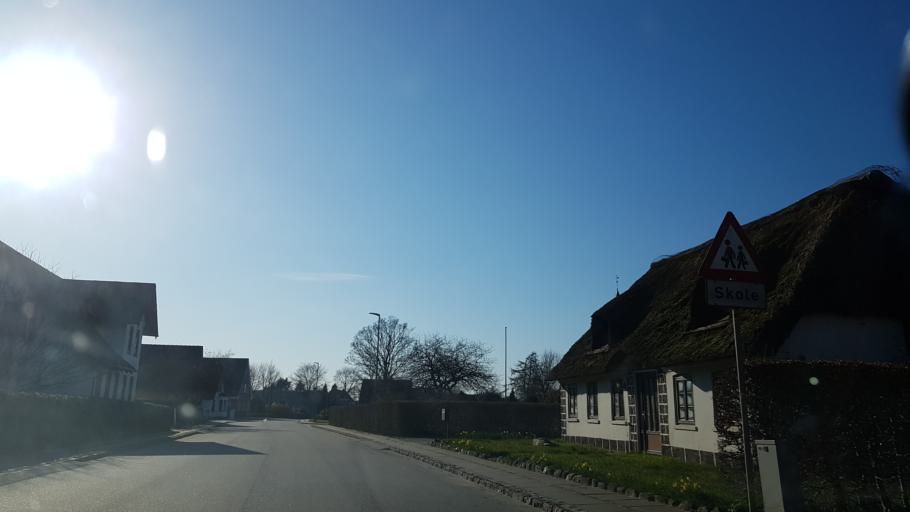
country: DK
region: South Denmark
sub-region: Vejen Kommune
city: Brorup
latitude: 55.4090
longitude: 8.9769
